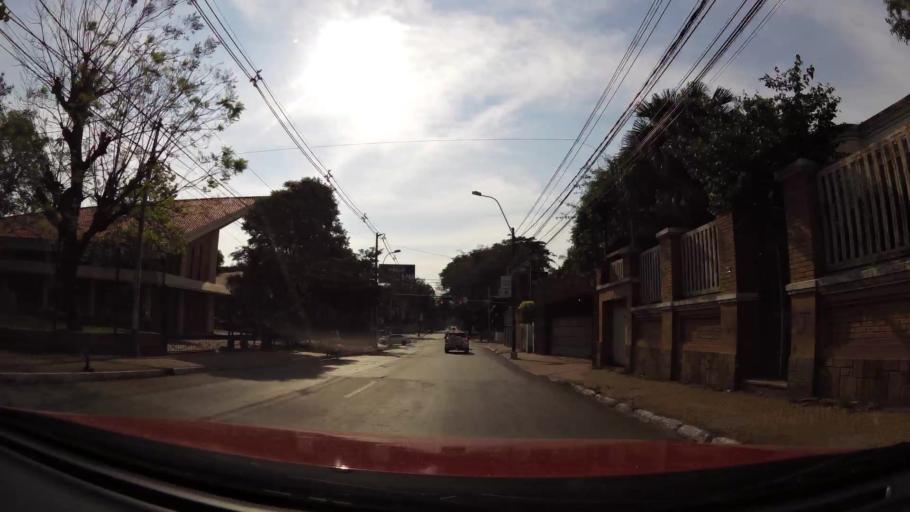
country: PY
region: Asuncion
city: Asuncion
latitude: -25.2875
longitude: -57.6101
